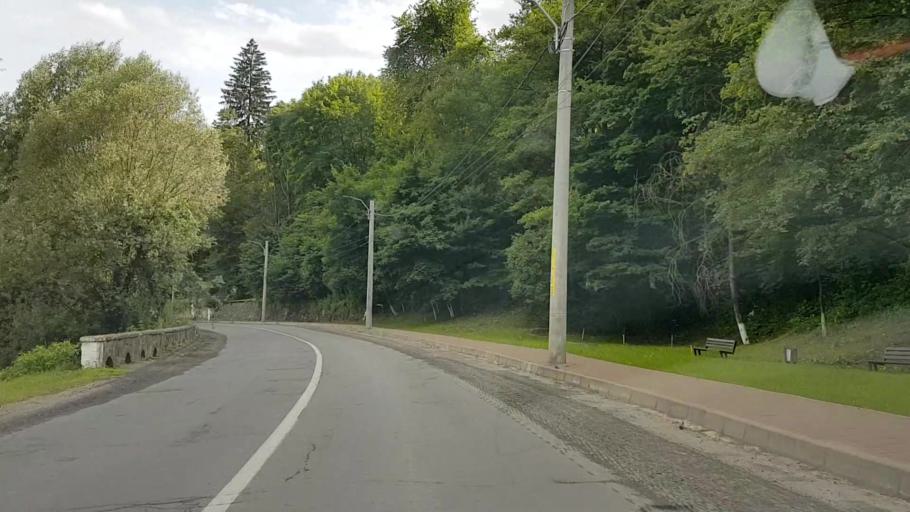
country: RO
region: Neamt
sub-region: Comuna Bicaz
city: Dodeni
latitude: 46.9181
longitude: 26.0842
